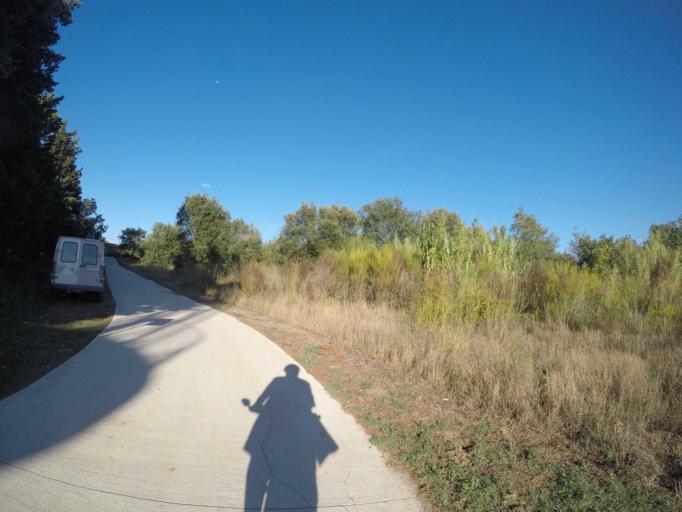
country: FR
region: Languedoc-Roussillon
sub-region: Departement des Pyrenees-Orientales
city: Sant Joan de Pladecorts
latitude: 42.5133
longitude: 2.7715
